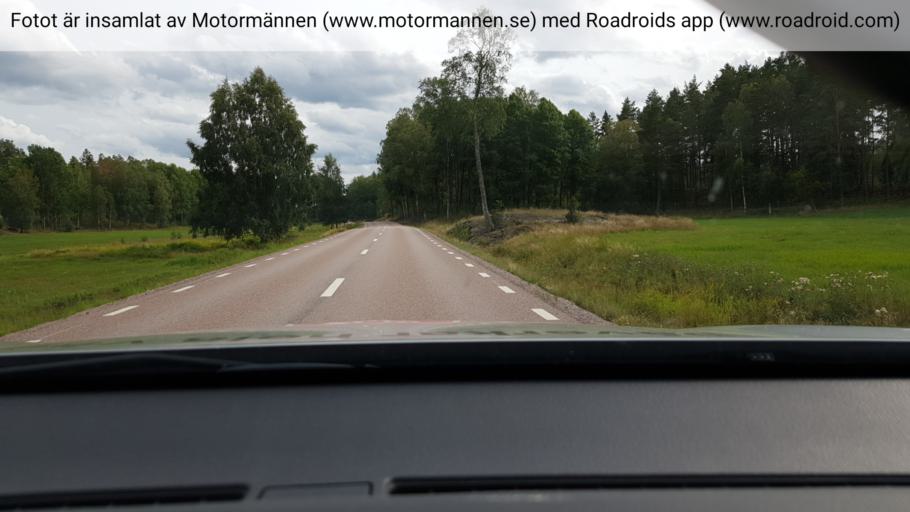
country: SE
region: Soedermanland
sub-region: Gnesta Kommun
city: Gnesta
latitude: 59.0137
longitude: 17.1723
